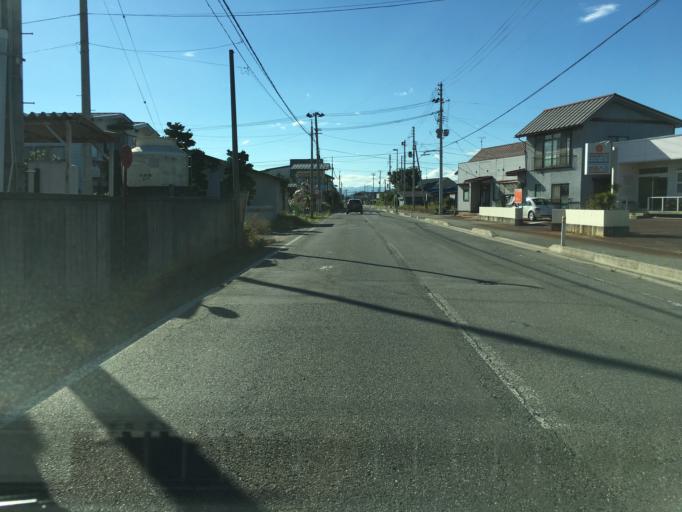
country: JP
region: Yamagata
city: Takahata
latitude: 37.9880
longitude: 140.1480
